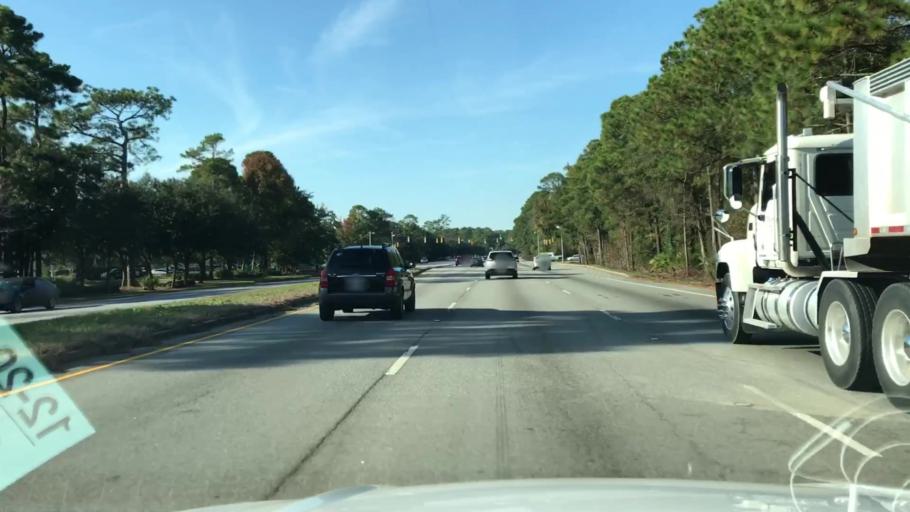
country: US
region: South Carolina
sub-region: Beaufort County
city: Bluffton
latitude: 32.2540
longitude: -80.8467
